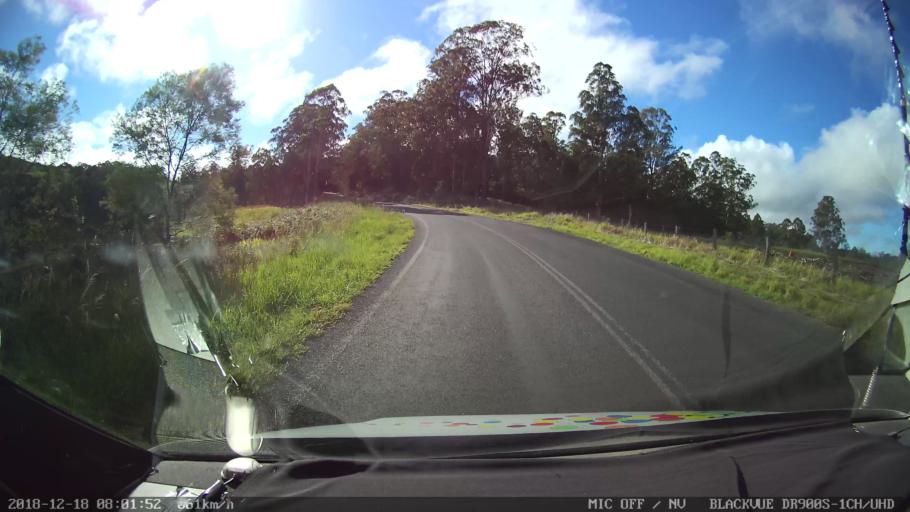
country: AU
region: New South Wales
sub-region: Kyogle
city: Kyogle
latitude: -28.3909
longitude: 152.6272
